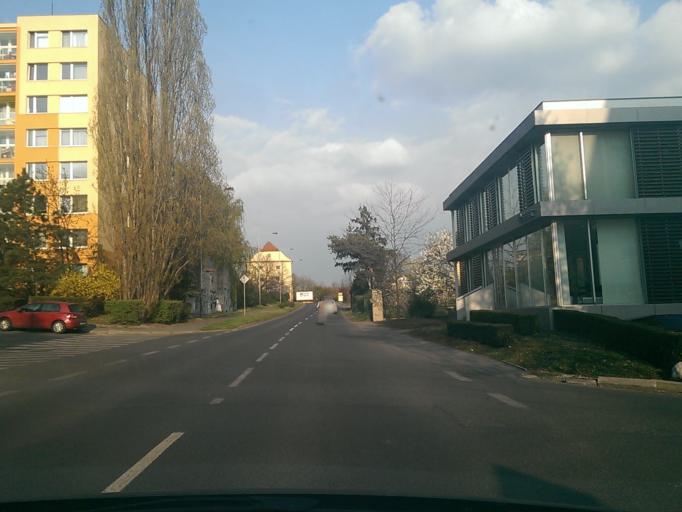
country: CZ
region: Praha
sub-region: Praha 9
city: Vysocany
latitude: 50.0530
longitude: 14.5039
